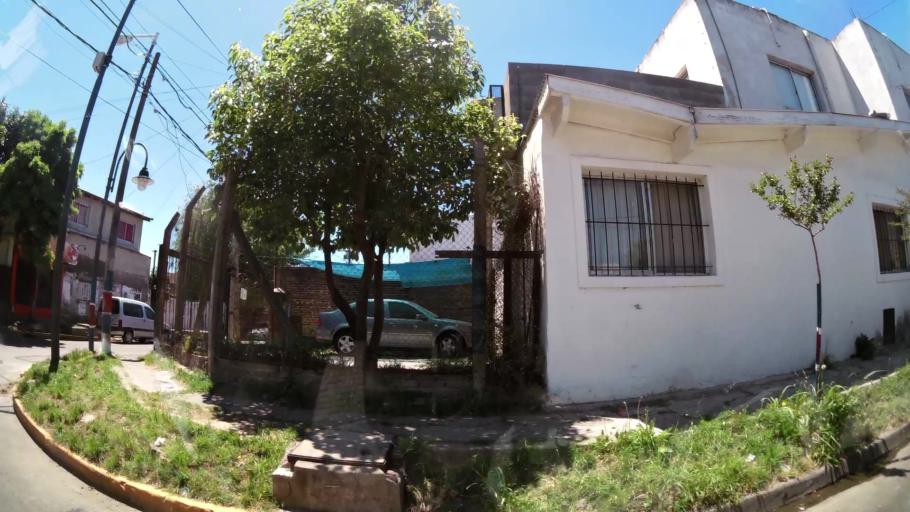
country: AR
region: Buenos Aires
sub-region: Partido de Tigre
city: Tigre
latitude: -34.4539
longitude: -58.5562
